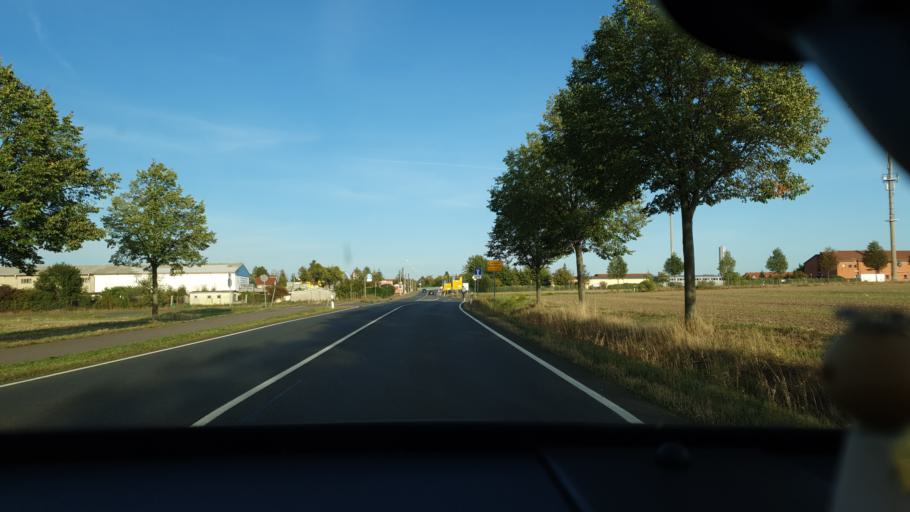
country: DE
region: Saxony
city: Eilenburg
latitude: 51.4588
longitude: 12.6056
